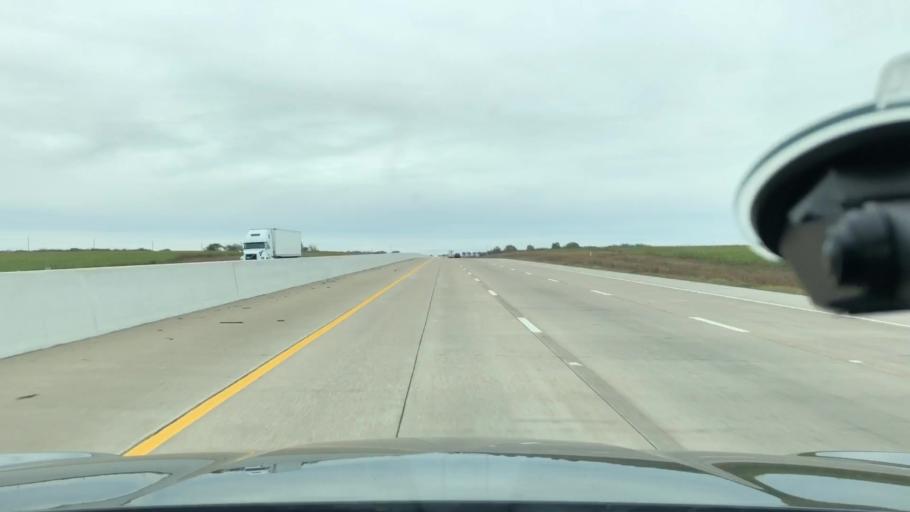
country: US
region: Texas
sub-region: Ellis County
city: Italy
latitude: 32.1517
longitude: -96.9311
